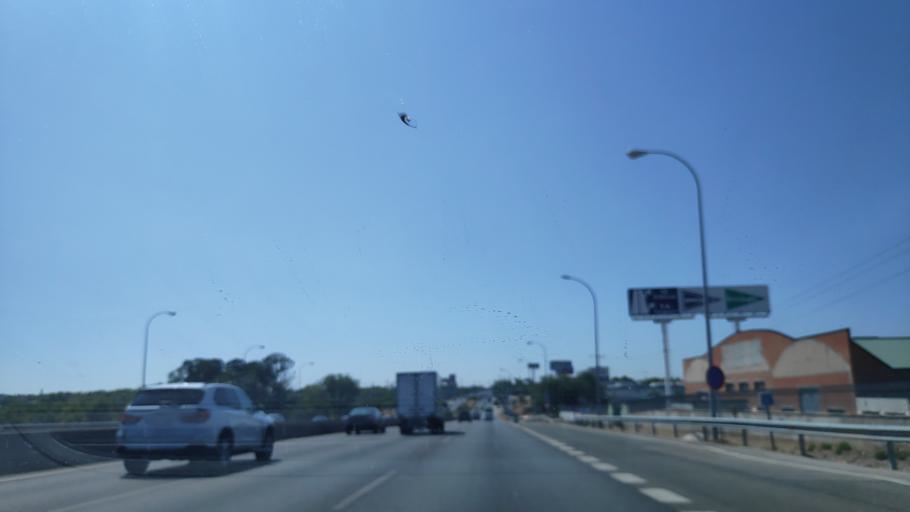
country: ES
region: Madrid
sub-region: Provincia de Madrid
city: Villaverde
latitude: 40.3552
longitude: -3.7221
